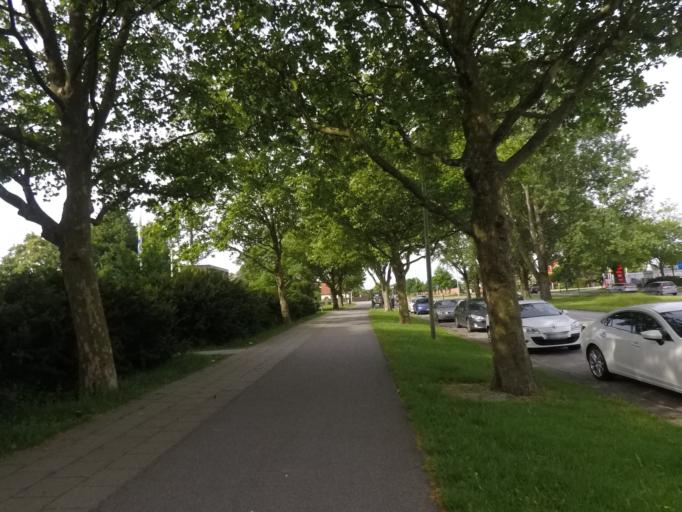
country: SE
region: Skane
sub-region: Malmo
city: Malmoe
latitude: 55.5804
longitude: 12.9773
